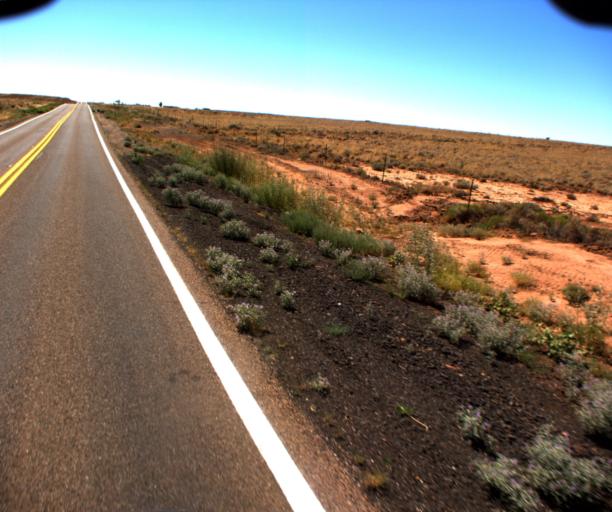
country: US
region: Arizona
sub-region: Navajo County
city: Winslow
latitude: 35.0028
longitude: -110.6865
